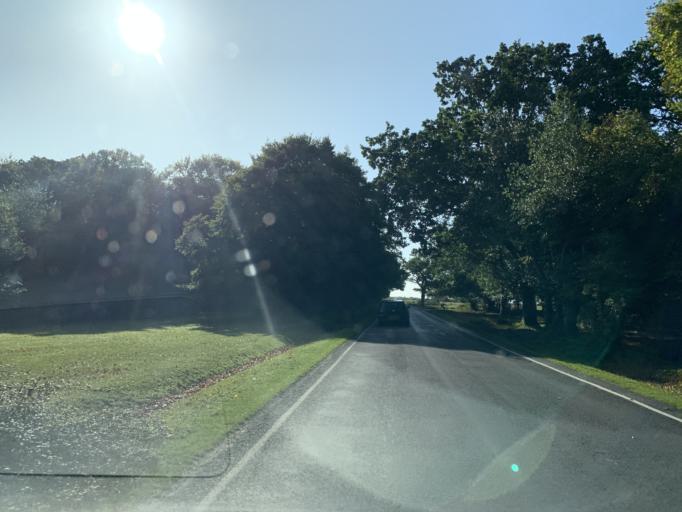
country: GB
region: England
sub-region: Hampshire
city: Cadnam
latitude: 50.9269
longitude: -1.6544
